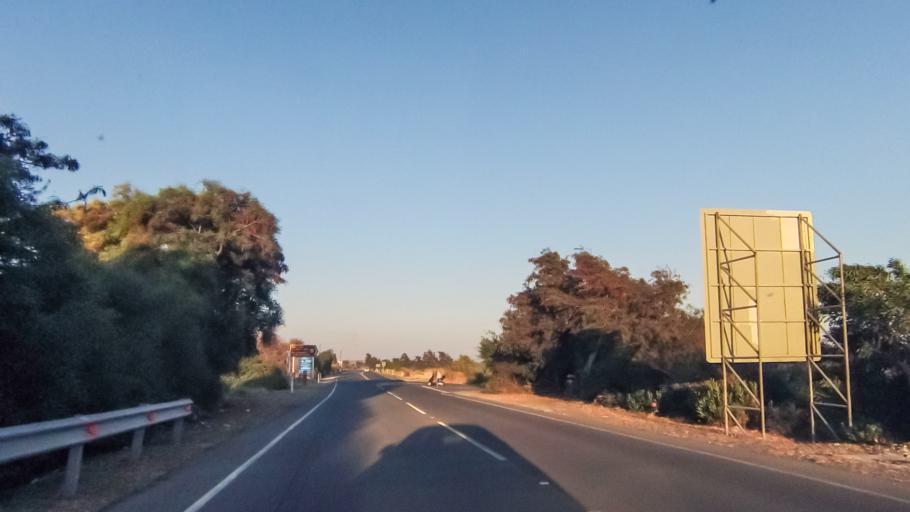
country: CY
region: Limassol
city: Erimi
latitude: 34.6647
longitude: 32.8935
